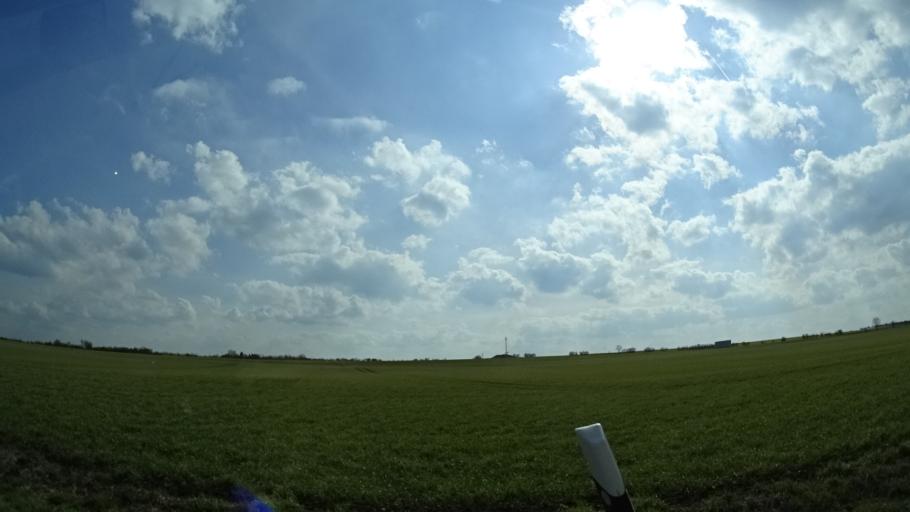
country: DE
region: Saxony-Anhalt
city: Leissling
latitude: 51.1563
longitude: 11.9027
